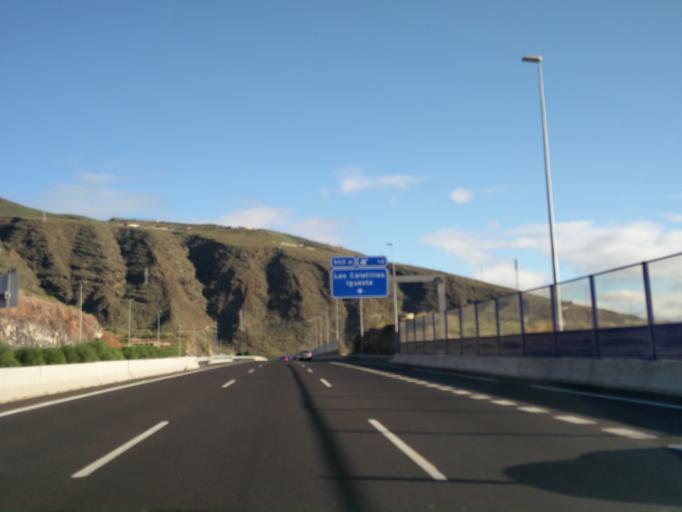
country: ES
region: Canary Islands
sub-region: Provincia de Santa Cruz de Tenerife
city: Candelaria
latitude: 28.3760
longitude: -16.3654
